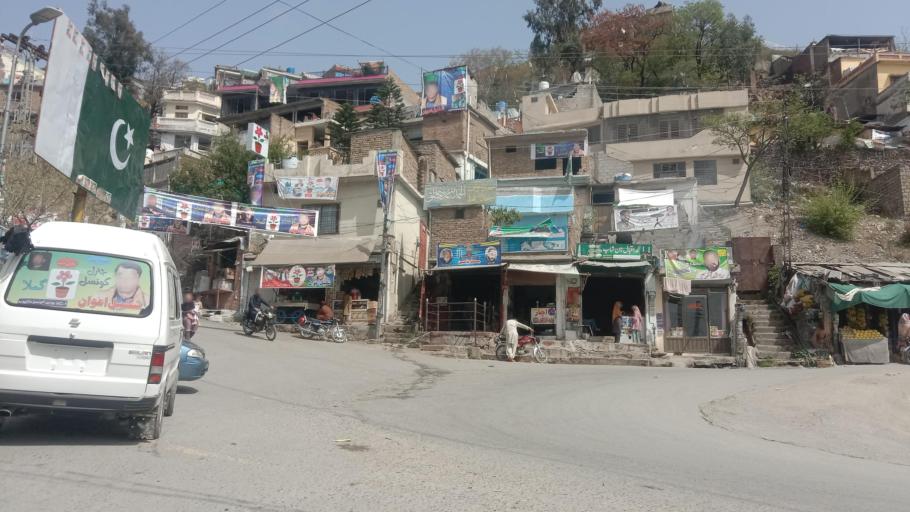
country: PK
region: Khyber Pakhtunkhwa
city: Abbottabad
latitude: 34.1509
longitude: 73.2022
